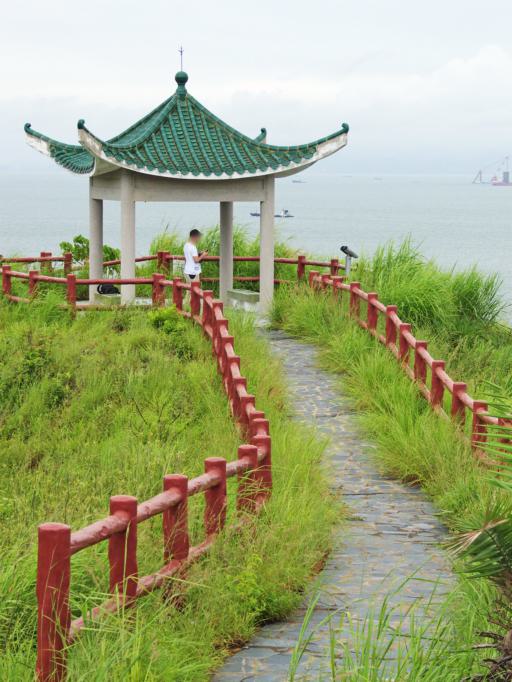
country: HK
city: Tai O
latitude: 22.2596
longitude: 113.8573
